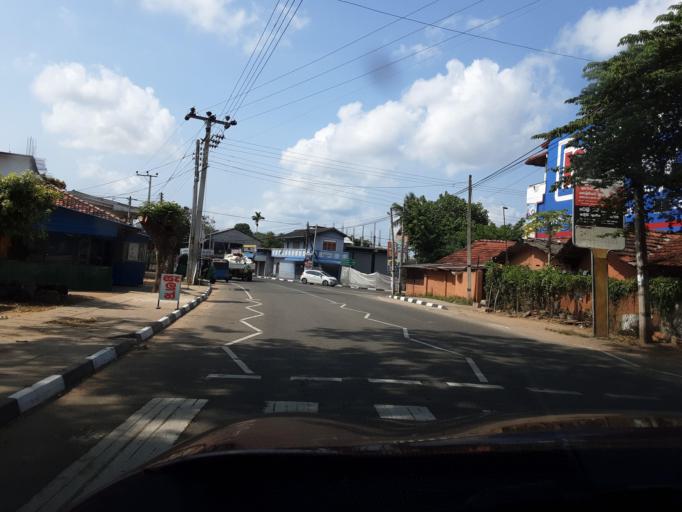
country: LK
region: Southern
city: Tangalla
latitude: 6.2973
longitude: 81.2367
